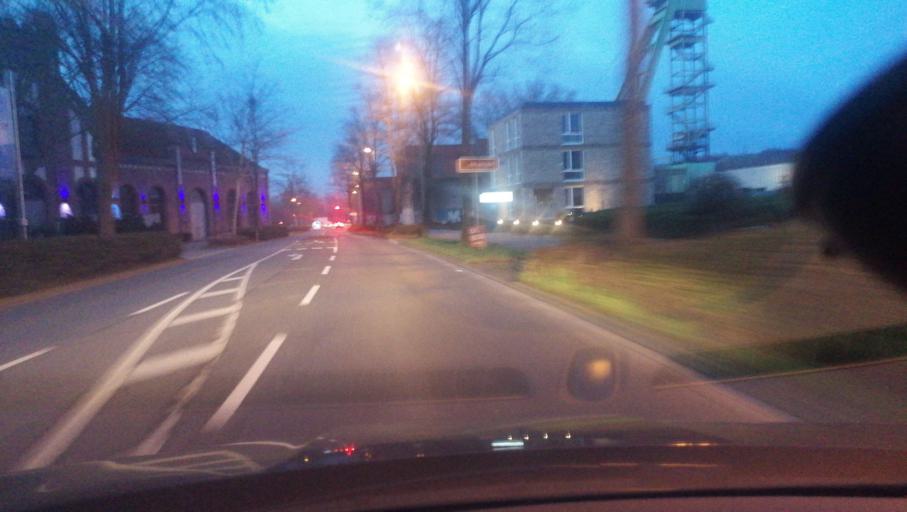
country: DE
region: North Rhine-Westphalia
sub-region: Regierungsbezirk Arnsberg
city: Dortmund
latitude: 51.5365
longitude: 7.4164
